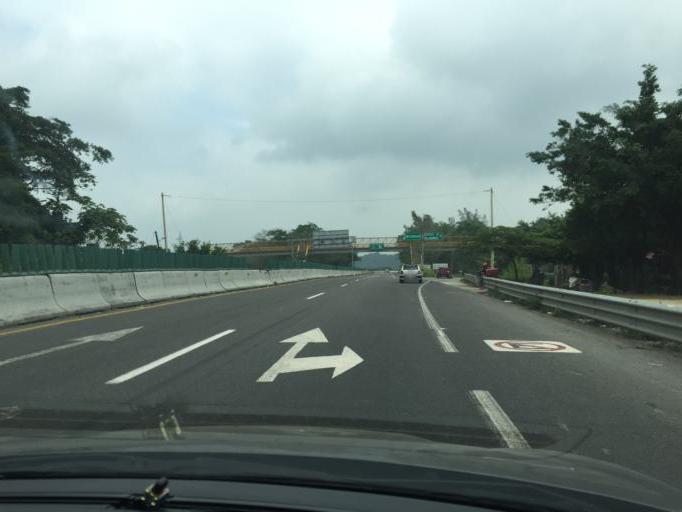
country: MX
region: Veracruz
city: Villa Nanchital
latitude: 18.0715
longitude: -94.3210
